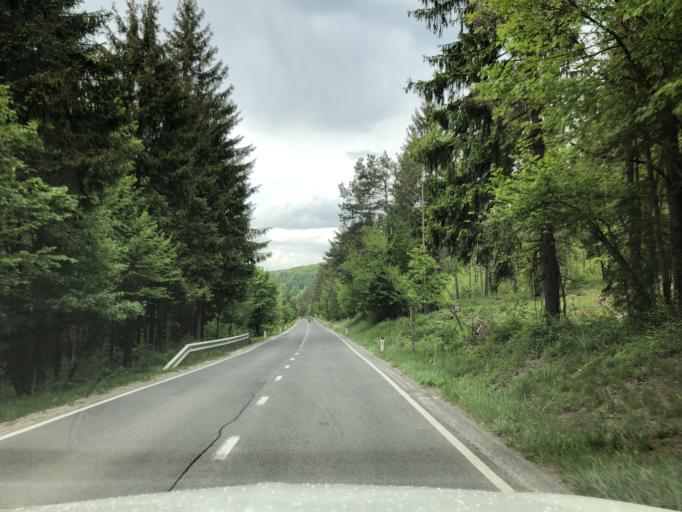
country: SI
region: Bloke
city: Nova Vas
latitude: 45.7608
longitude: 14.4618
